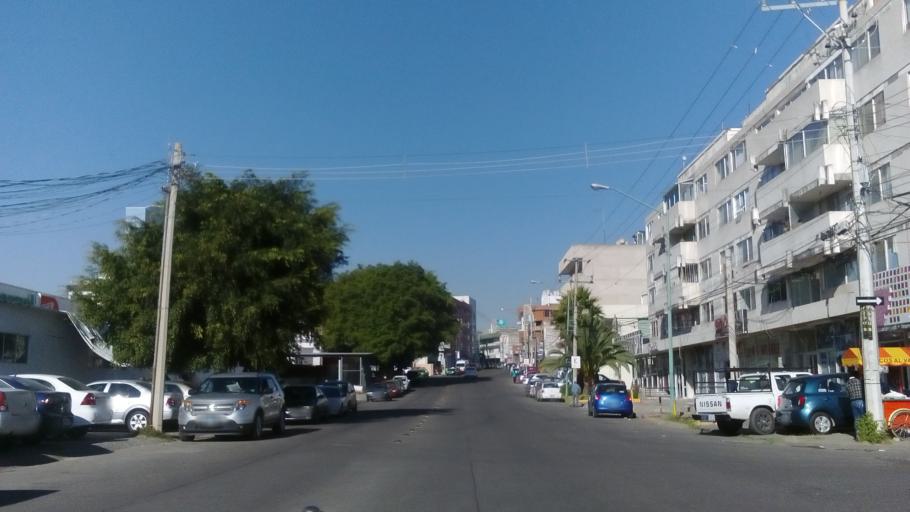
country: MX
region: Guanajuato
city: Leon
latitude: 21.1427
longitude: -101.6867
